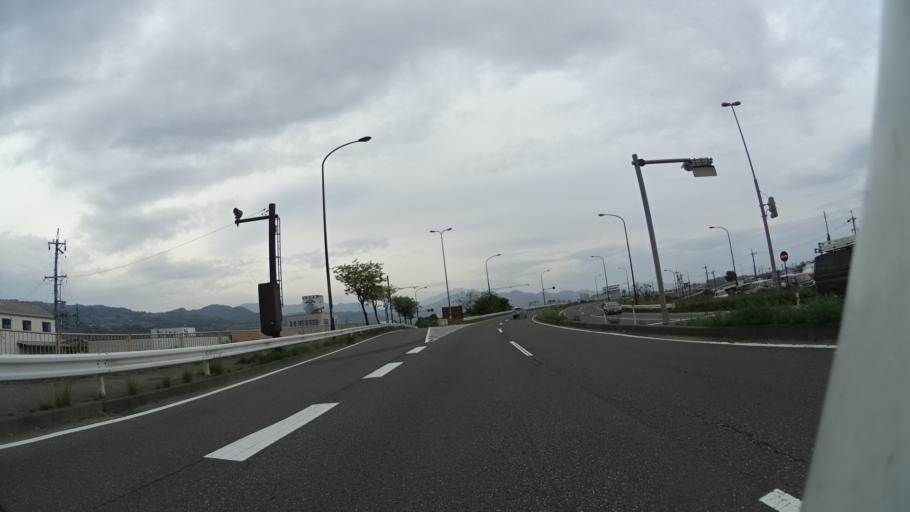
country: JP
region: Nagano
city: Nagano-shi
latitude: 36.5605
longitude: 138.1382
